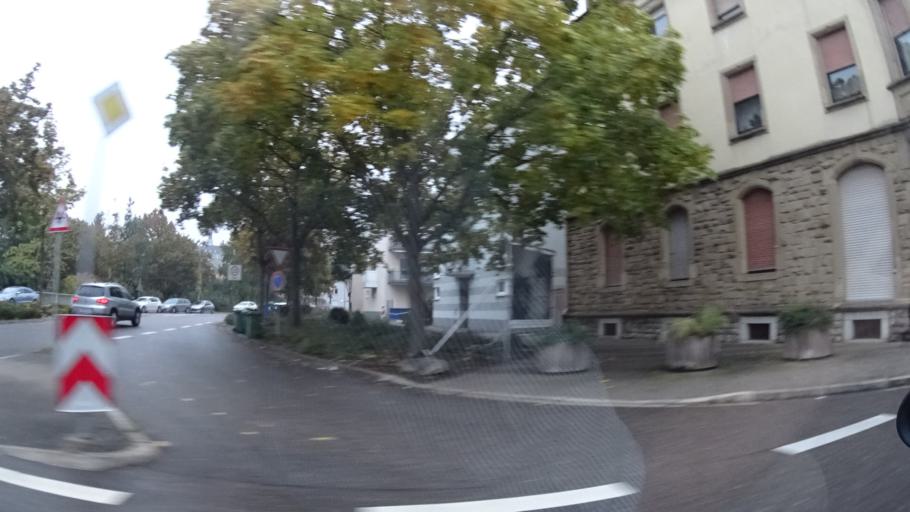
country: DE
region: Baden-Wuerttemberg
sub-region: Karlsruhe Region
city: Bruchsal
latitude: 49.1220
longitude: 8.6036
